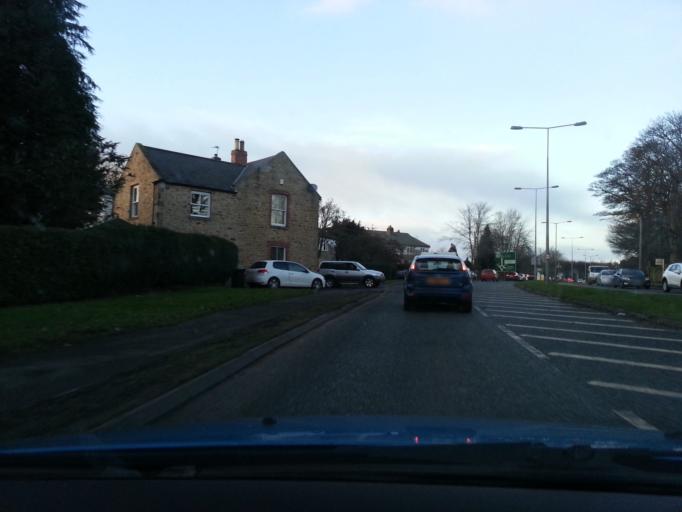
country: GB
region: England
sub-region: County Durham
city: Durham
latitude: 54.7862
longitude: -1.5970
